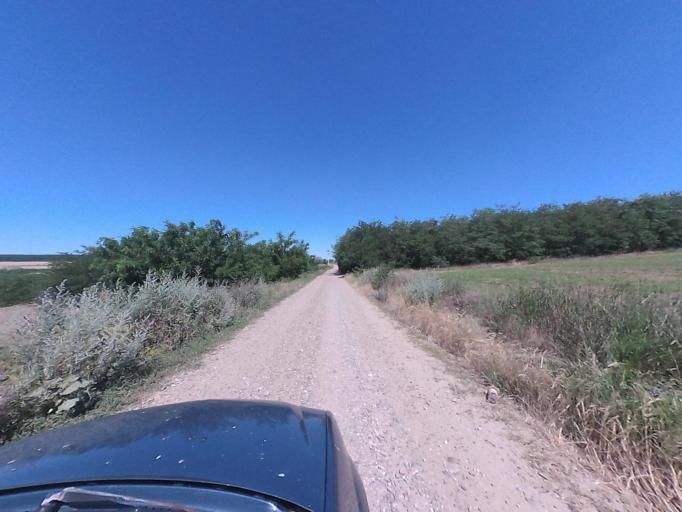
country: RO
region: Vaslui
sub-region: Comuna Costesti
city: Costesti
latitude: 46.4842
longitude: 27.7720
